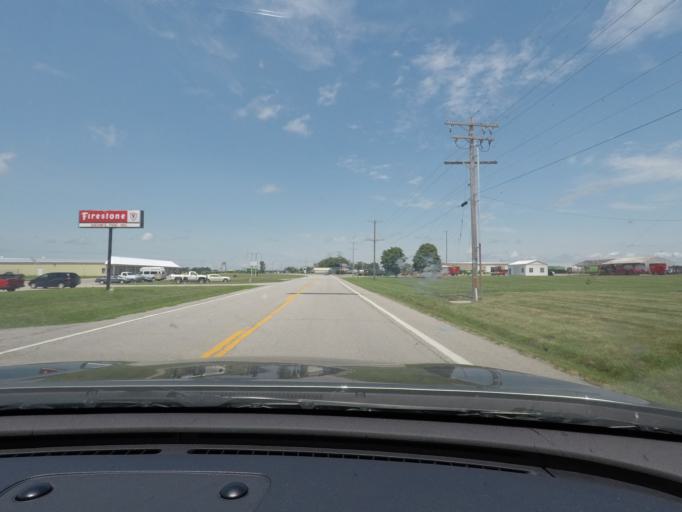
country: US
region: Missouri
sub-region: Saline County
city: Marshall
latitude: 39.1339
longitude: -93.2229
